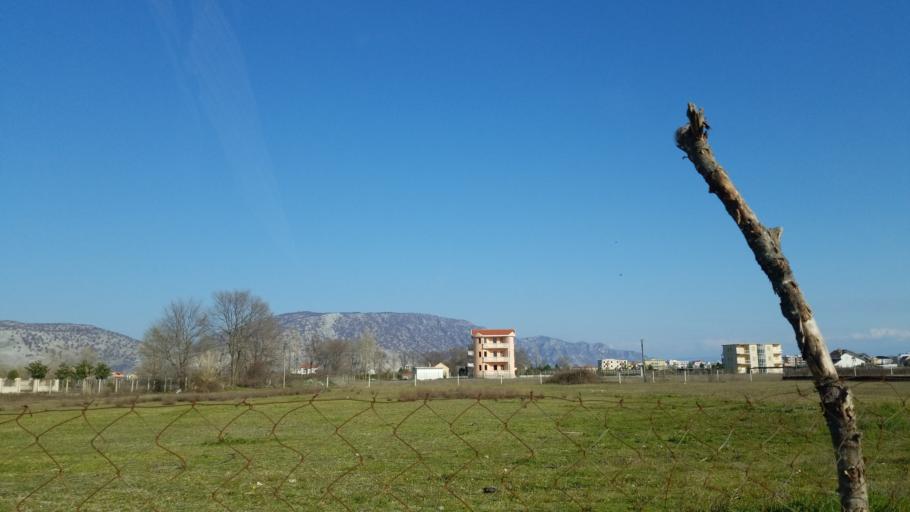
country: AL
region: Shkoder
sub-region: Rrethi i Shkodres
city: Velipoje
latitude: 41.8709
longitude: 19.4146
